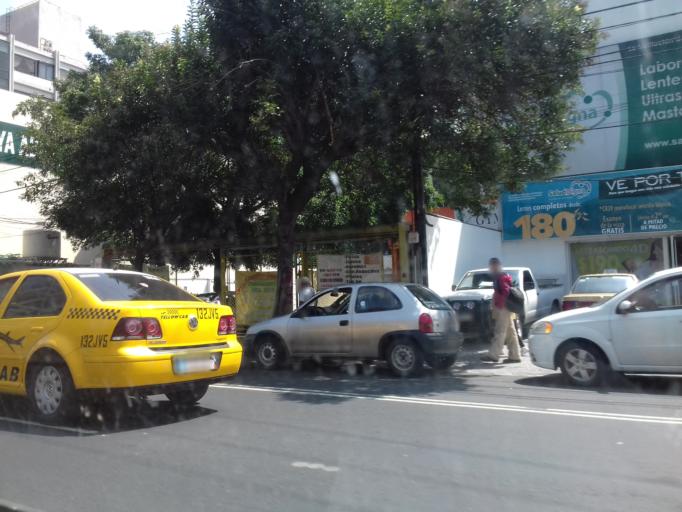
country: MX
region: Mexico City
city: Coyoacan
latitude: 19.3583
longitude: -99.1722
